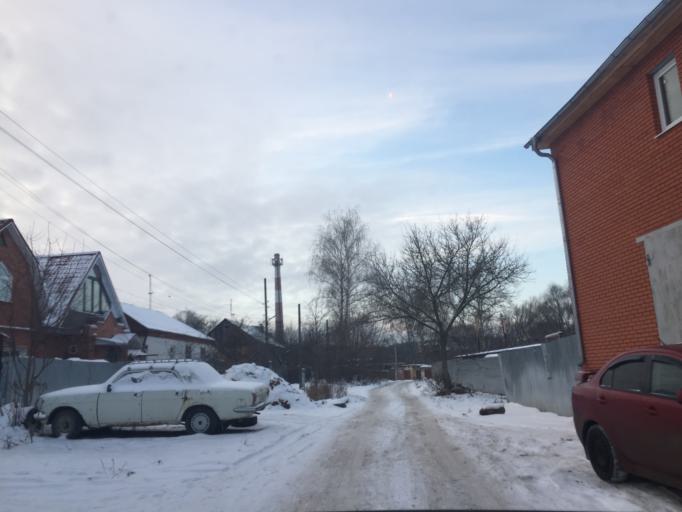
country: RU
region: Tula
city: Gorelki
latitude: 54.2308
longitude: 37.6331
